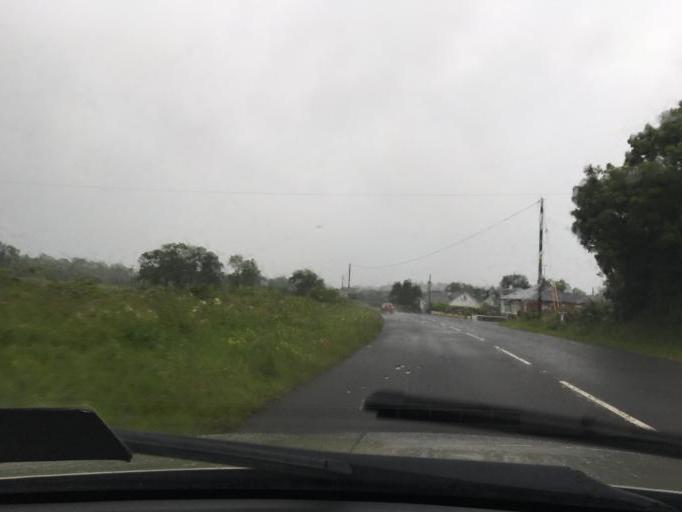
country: GB
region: Northern Ireland
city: Irvinestown
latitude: 54.5468
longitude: -7.8126
